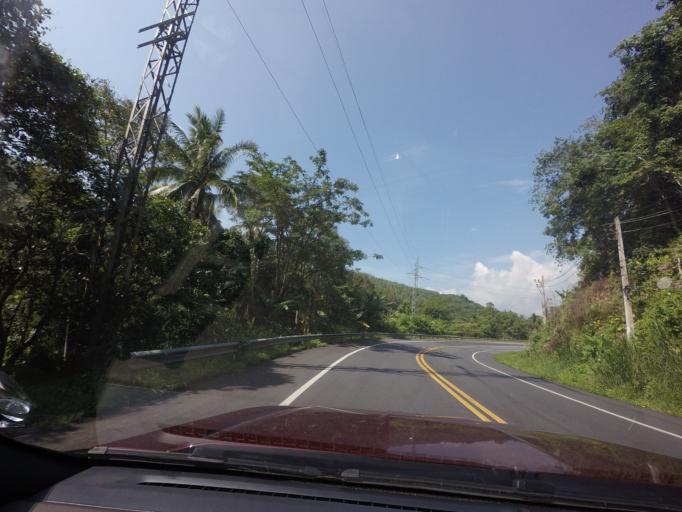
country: TH
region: Yala
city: Than To
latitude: 5.9666
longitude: 101.2004
